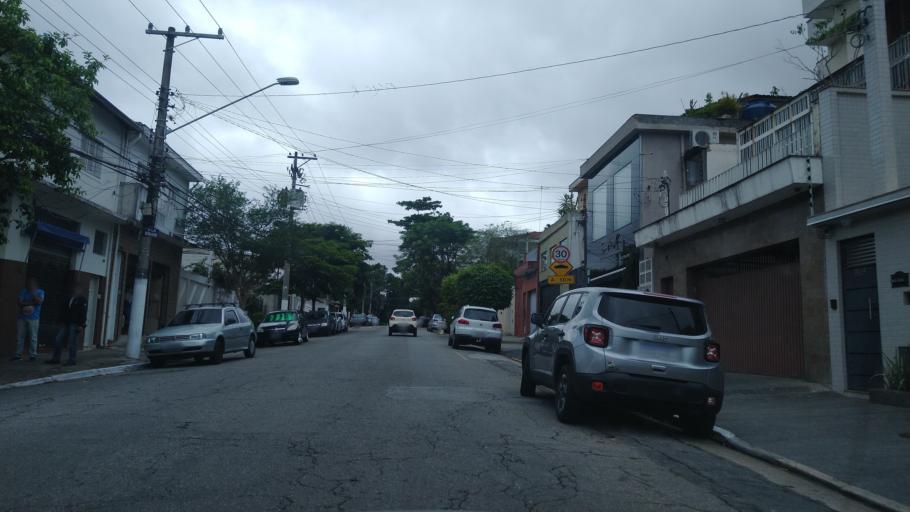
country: BR
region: Sao Paulo
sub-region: Sao Paulo
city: Sao Paulo
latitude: -23.4795
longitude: -46.6211
